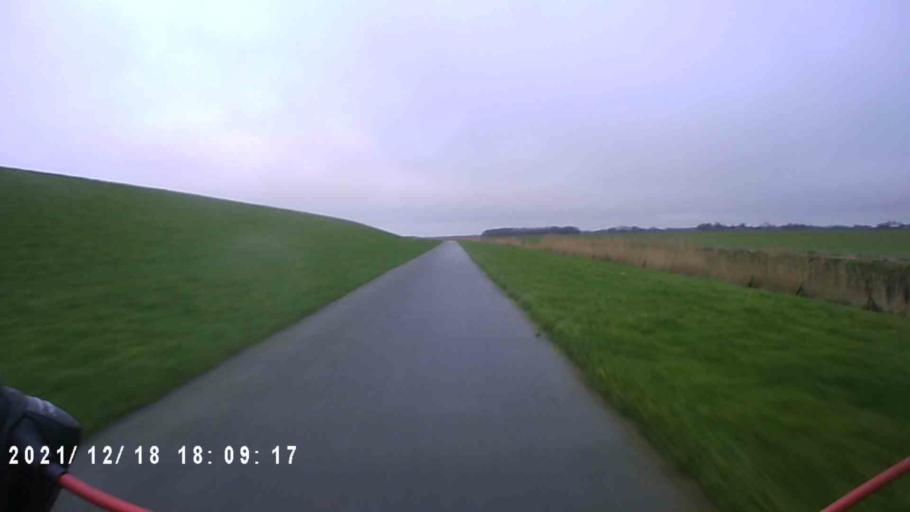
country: NL
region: Friesland
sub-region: Gemeente Dongeradeel
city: Holwerd
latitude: 53.3866
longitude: 5.9293
